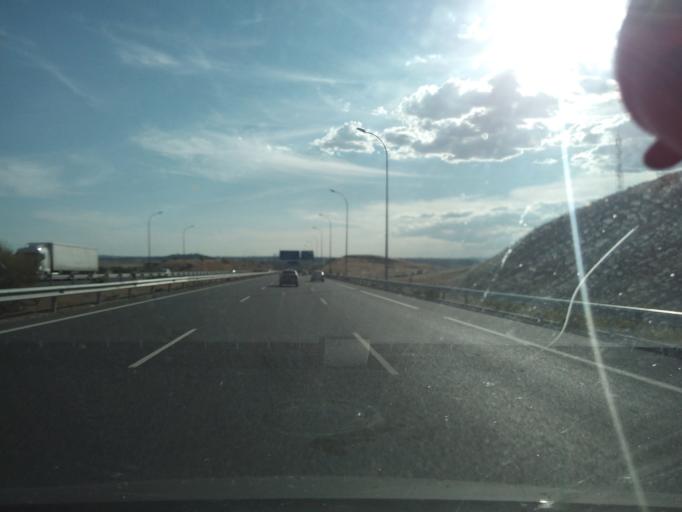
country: ES
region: Madrid
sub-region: Provincia de Madrid
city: Villa de Vallecas
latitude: 40.3402
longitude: -3.6042
